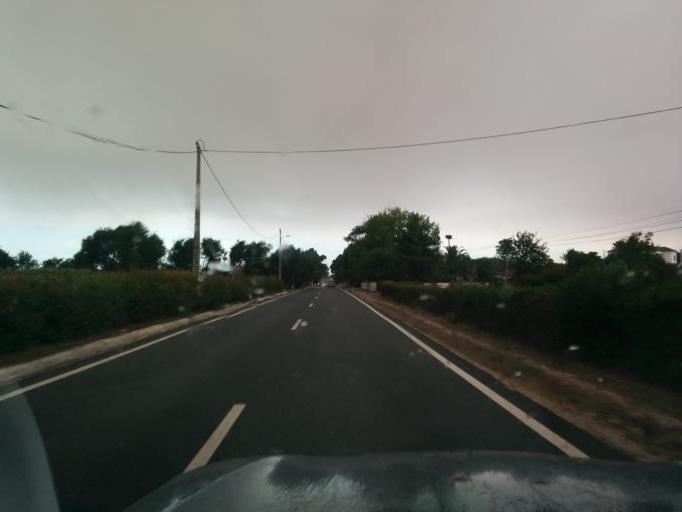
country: PT
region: Beja
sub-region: Odemira
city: Vila Nova de Milfontes
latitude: 37.6478
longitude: -8.7595
